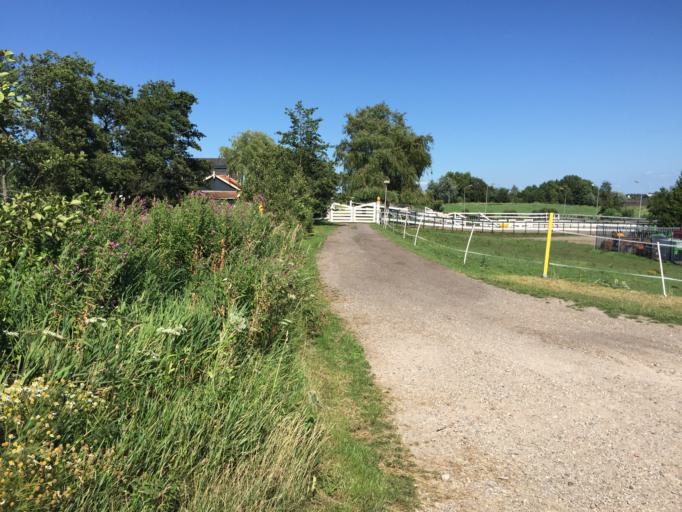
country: NL
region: North Holland
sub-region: Gemeente Uithoorn
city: Uithoorn
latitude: 52.2375
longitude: 4.8501
